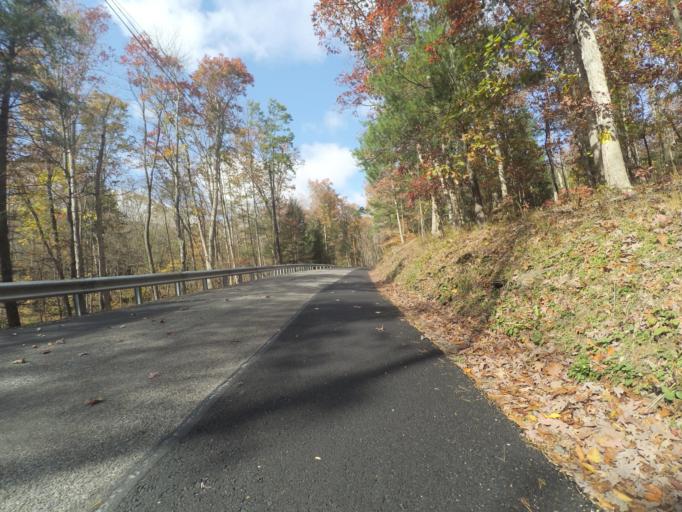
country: US
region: Pennsylvania
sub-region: Centre County
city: Stormstown
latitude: 40.8571
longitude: -77.9823
